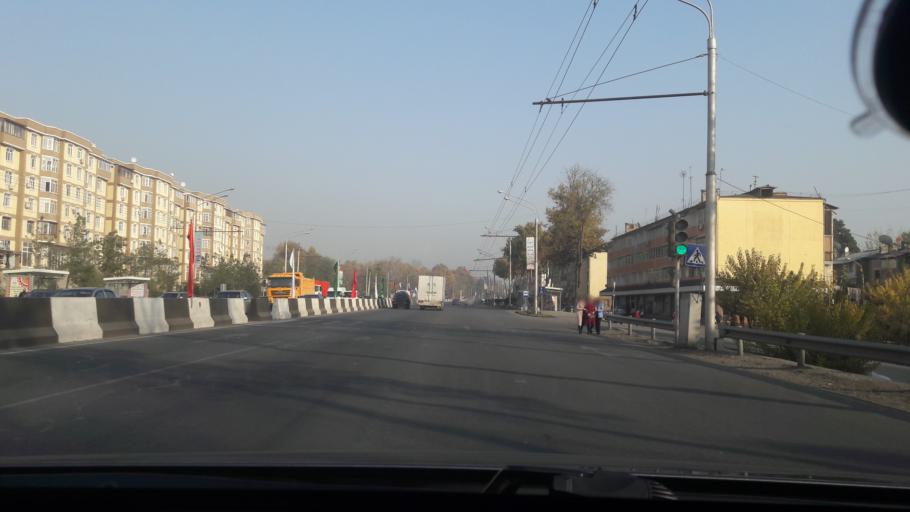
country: TJ
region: Dushanbe
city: Dushanbe
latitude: 38.5532
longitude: 68.8503
